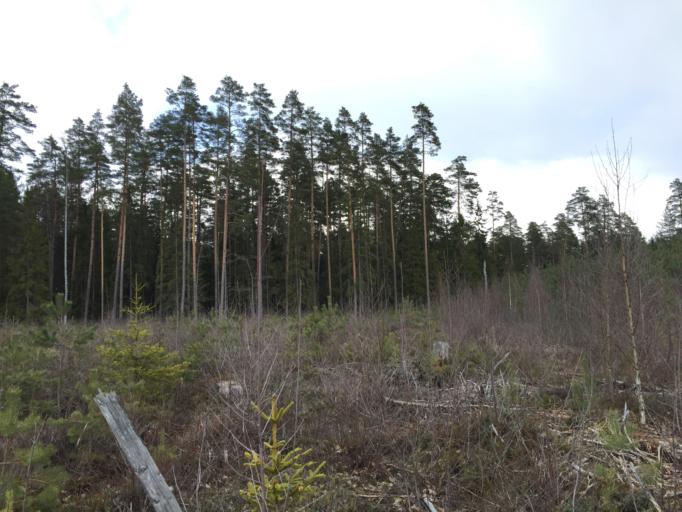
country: LV
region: Garkalne
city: Garkalne
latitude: 56.9597
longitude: 24.4930
